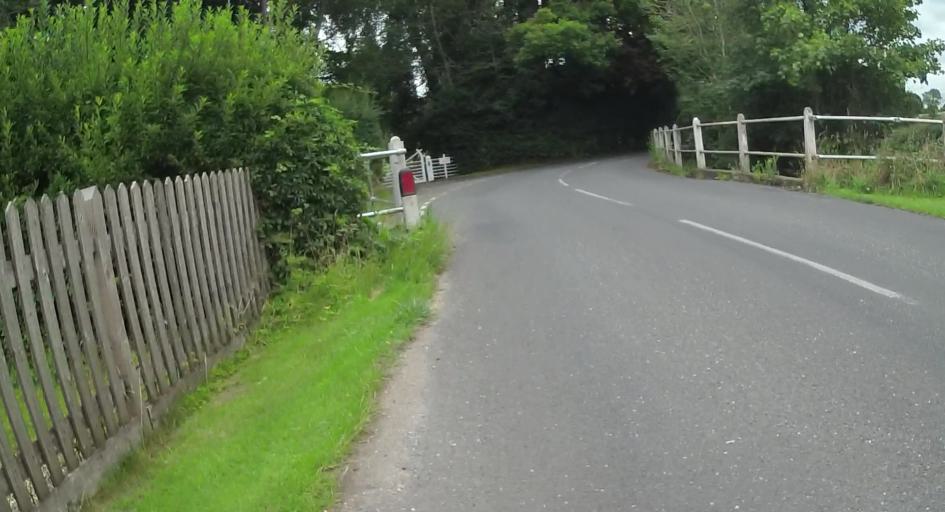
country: GB
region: England
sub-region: Hampshire
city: Swanmore
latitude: 51.0520
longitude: -1.1690
